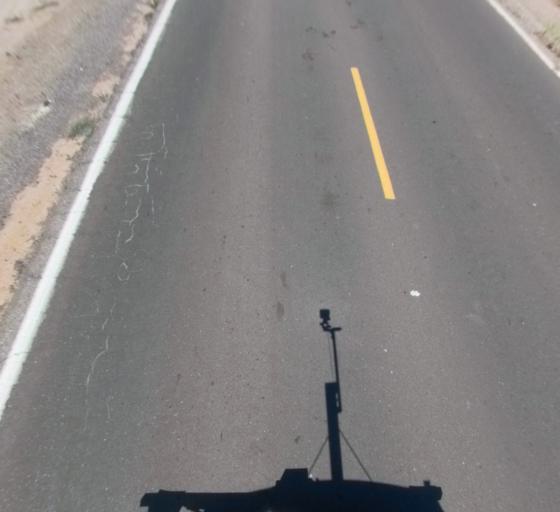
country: US
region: California
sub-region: Madera County
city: Parkwood
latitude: 36.8512
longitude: -120.1409
